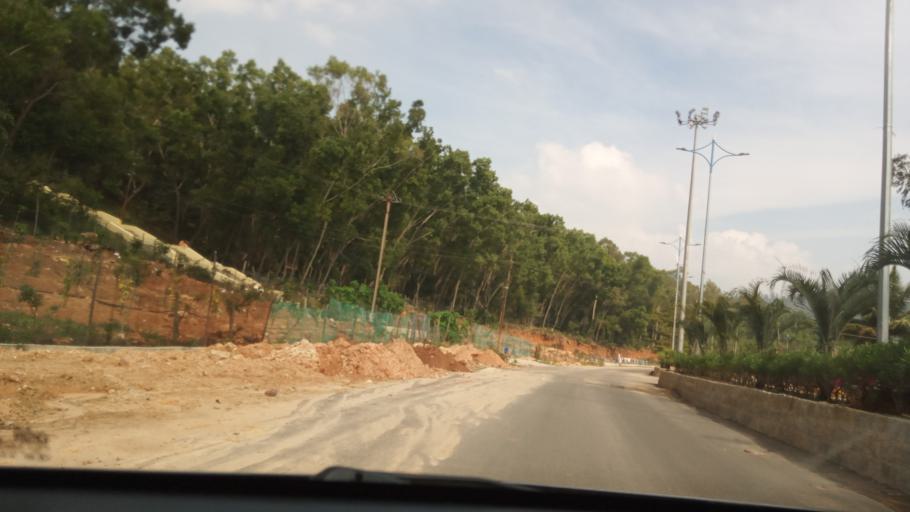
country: IN
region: Andhra Pradesh
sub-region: Chittoor
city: Tirumala
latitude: 13.6917
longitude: 79.3465
